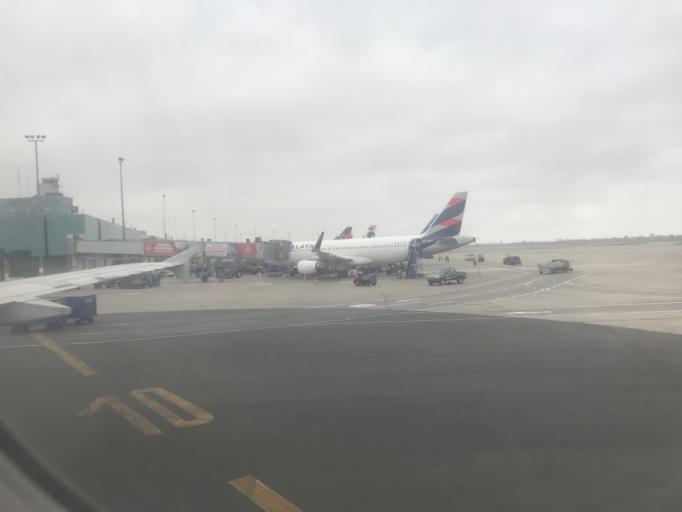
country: PE
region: Callao
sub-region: Callao
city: Callao
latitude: -12.0213
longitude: -77.1109
